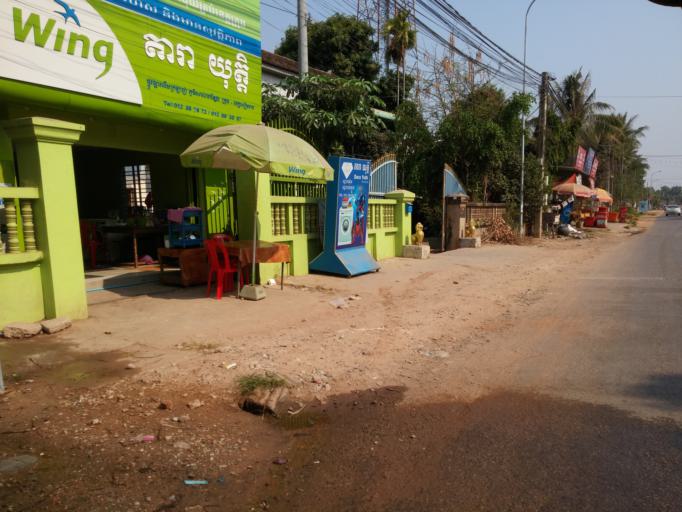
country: KH
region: Siem Reap
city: Siem Reap
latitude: 13.3696
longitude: 103.8490
